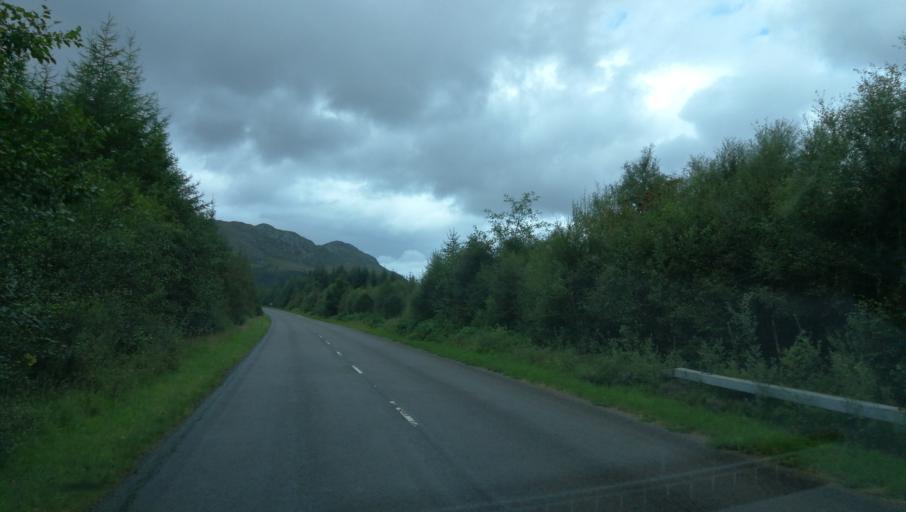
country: GB
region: Scotland
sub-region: Highland
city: Ullapool
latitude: 57.6867
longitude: -5.5480
